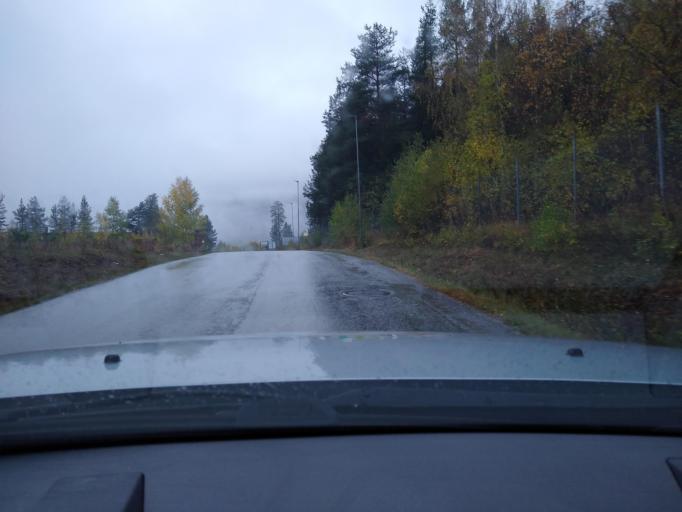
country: NO
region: Oppland
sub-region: Ringebu
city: Ringebu
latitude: 61.5491
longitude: 10.0618
